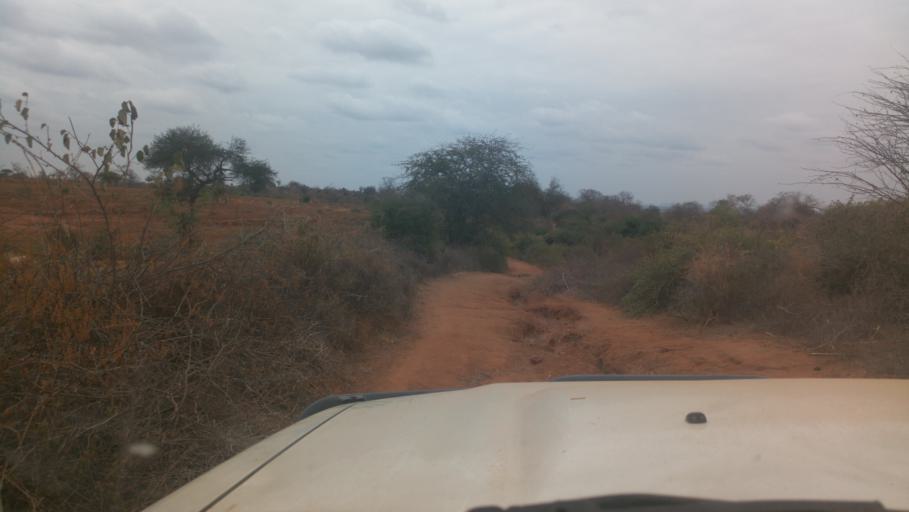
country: KE
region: Makueni
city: Makueni
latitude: -1.9696
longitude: 38.0761
